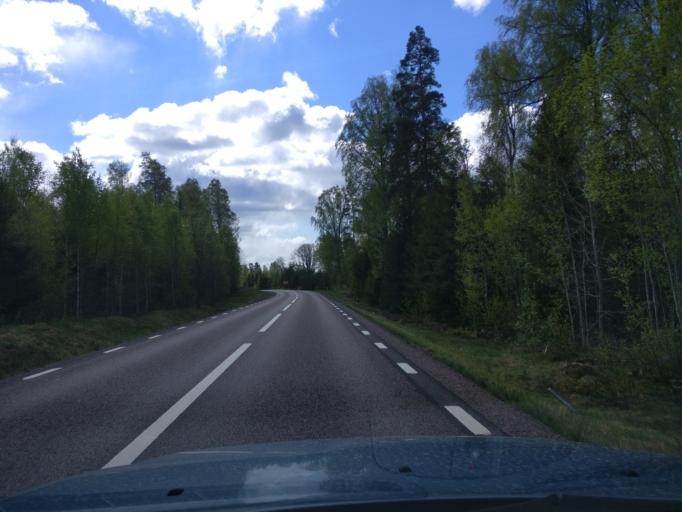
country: SE
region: Vaermland
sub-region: Karlstads Kommun
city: Molkom
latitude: 59.7416
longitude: 13.6786
